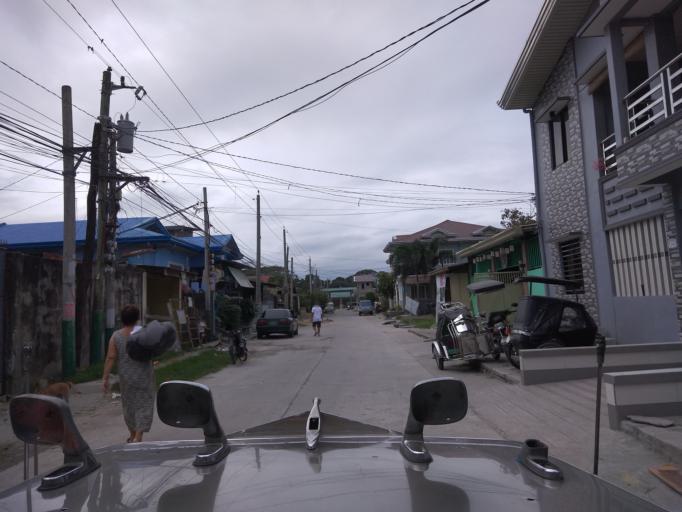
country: PH
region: Central Luzon
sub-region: Province of Pampanga
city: Mexico
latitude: 15.0633
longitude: 120.7175
